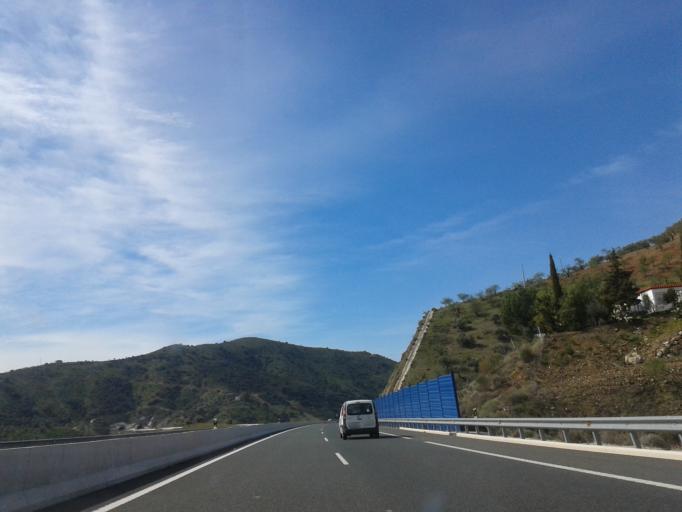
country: ES
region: Andalusia
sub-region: Provincia de Malaga
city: Casabermeja
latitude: 36.8824
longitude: -4.4744
